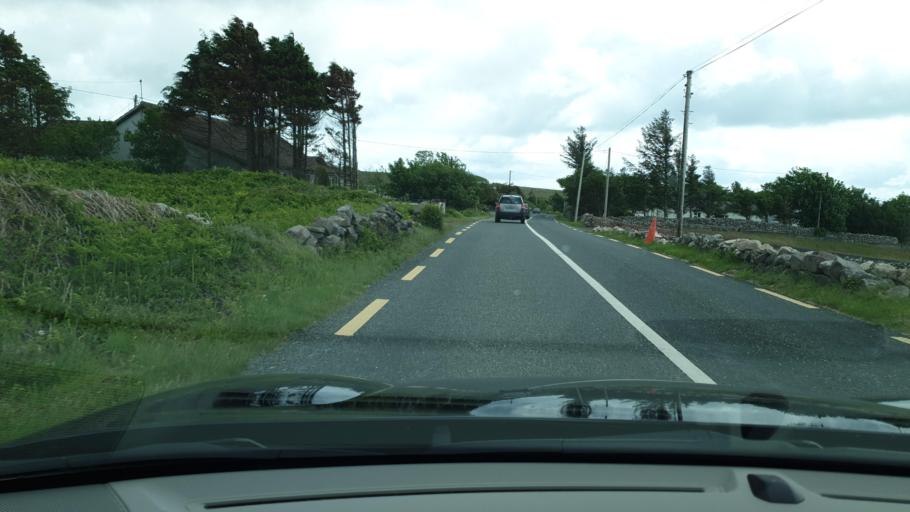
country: IE
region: Connaught
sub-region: County Galway
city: Oughterard
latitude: 53.2739
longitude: -9.5258
